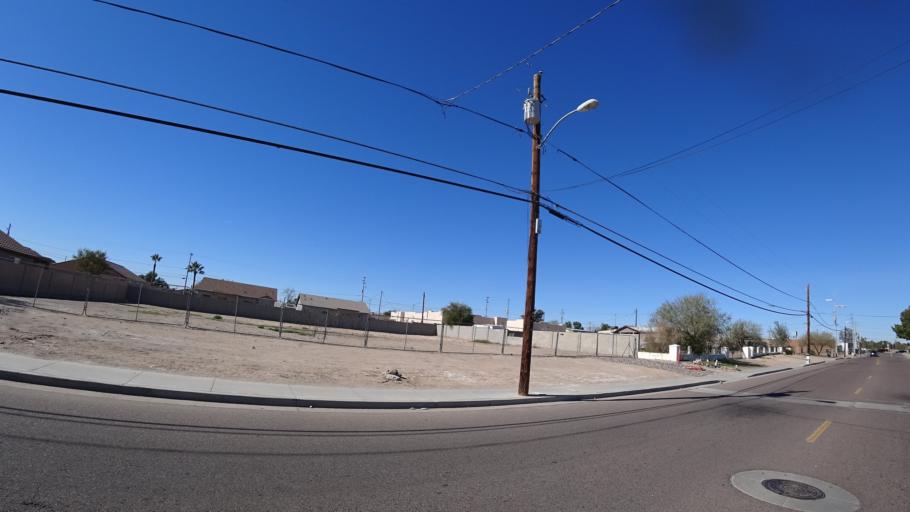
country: US
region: Arizona
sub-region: Maricopa County
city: Avondale
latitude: 33.4294
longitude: -112.3452
